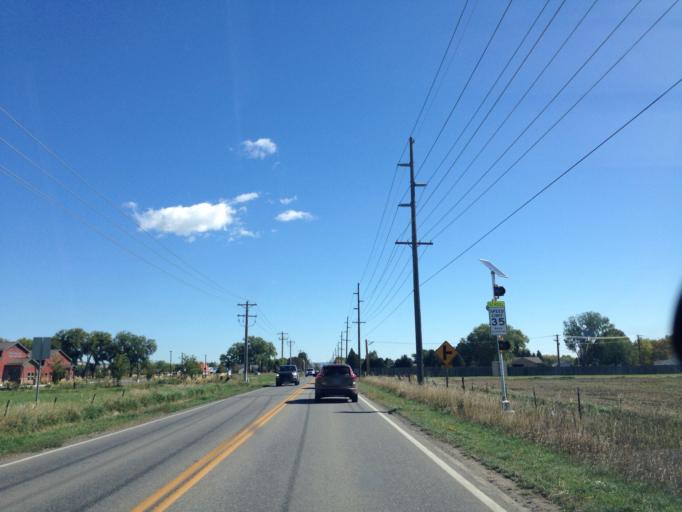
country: US
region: Montana
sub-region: Yellowstone County
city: Billings
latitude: 45.7841
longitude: -108.6414
